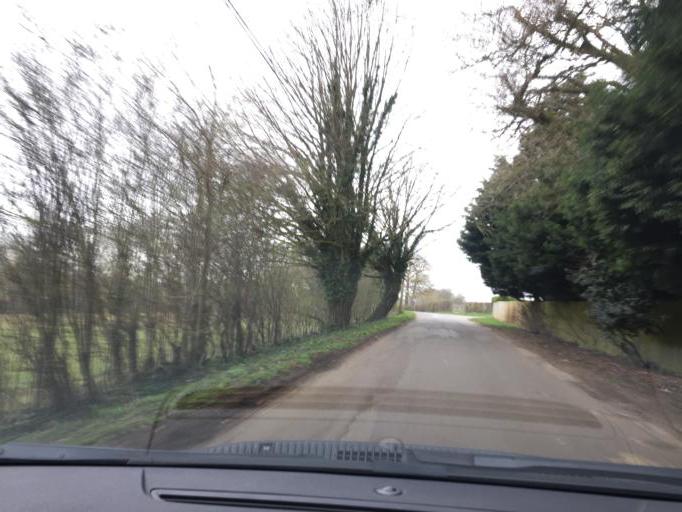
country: GB
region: England
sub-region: Oxfordshire
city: Deddington
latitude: 51.9537
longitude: -1.3686
